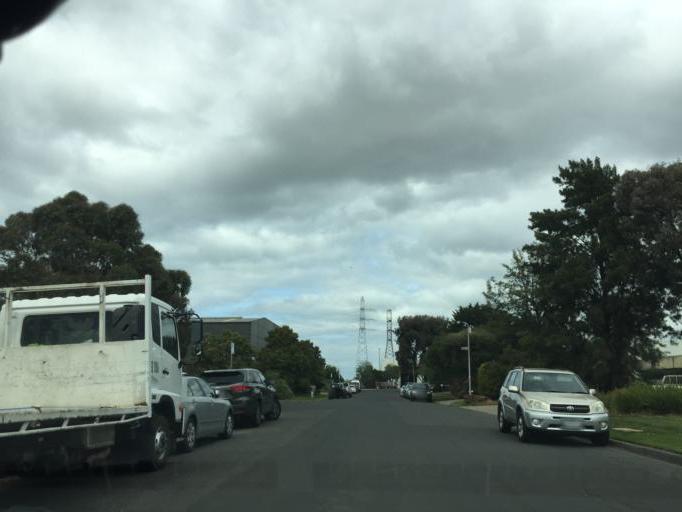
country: AU
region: Victoria
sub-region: Brimbank
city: Brooklyn
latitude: -37.8221
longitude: 144.8548
